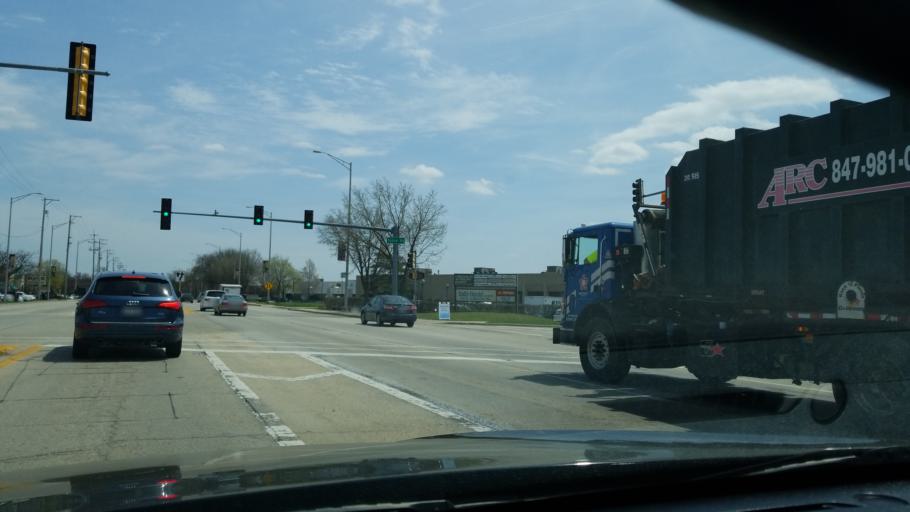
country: US
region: Illinois
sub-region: Cook County
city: Elk Grove Village
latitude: 42.0433
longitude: -87.9808
